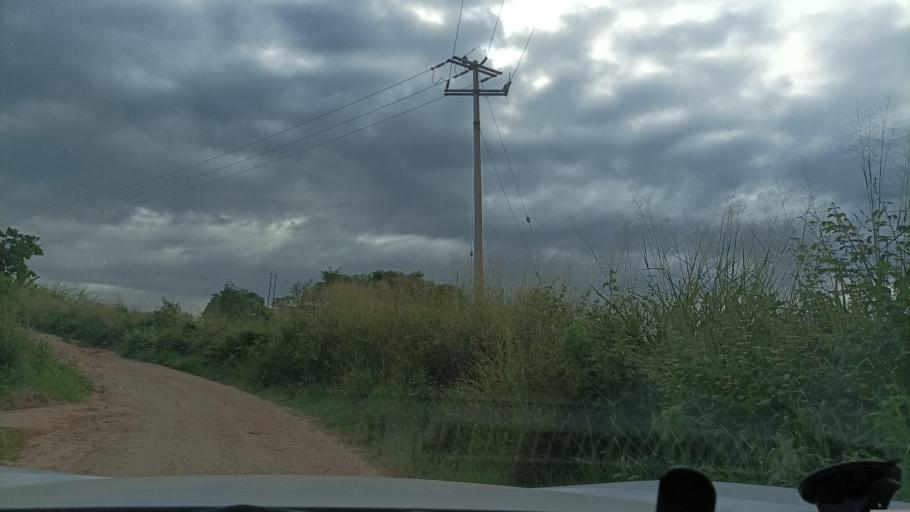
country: MX
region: Veracruz
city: Oluta
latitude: 17.9336
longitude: -94.8835
